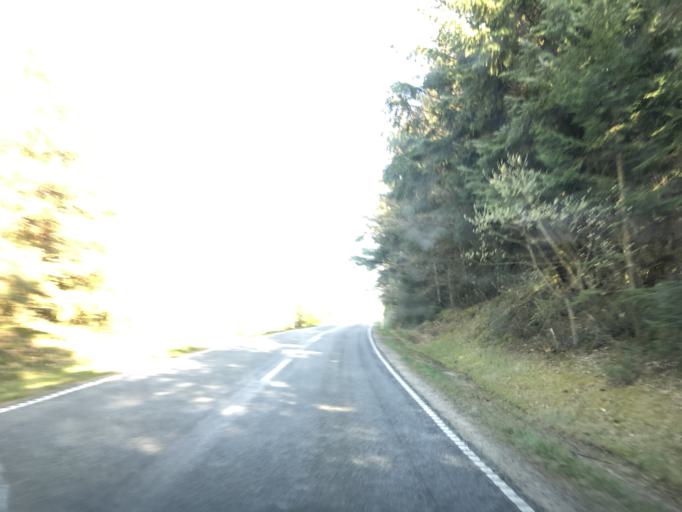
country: DK
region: Central Jutland
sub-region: Holstebro Kommune
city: Ulfborg
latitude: 56.1941
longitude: 8.3341
